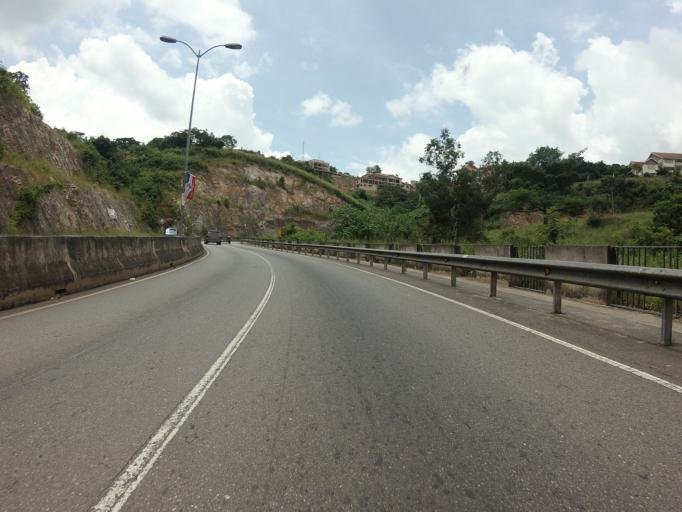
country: GH
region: Eastern
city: Aburi
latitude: 5.7937
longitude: -0.1862
